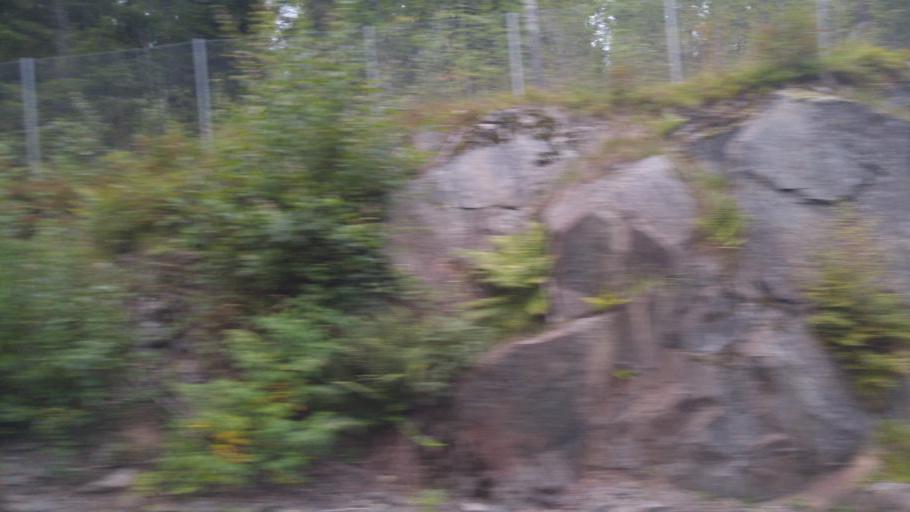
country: NO
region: Oslo
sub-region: Oslo
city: Sjolyststranda
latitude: 59.9616
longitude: 10.6873
